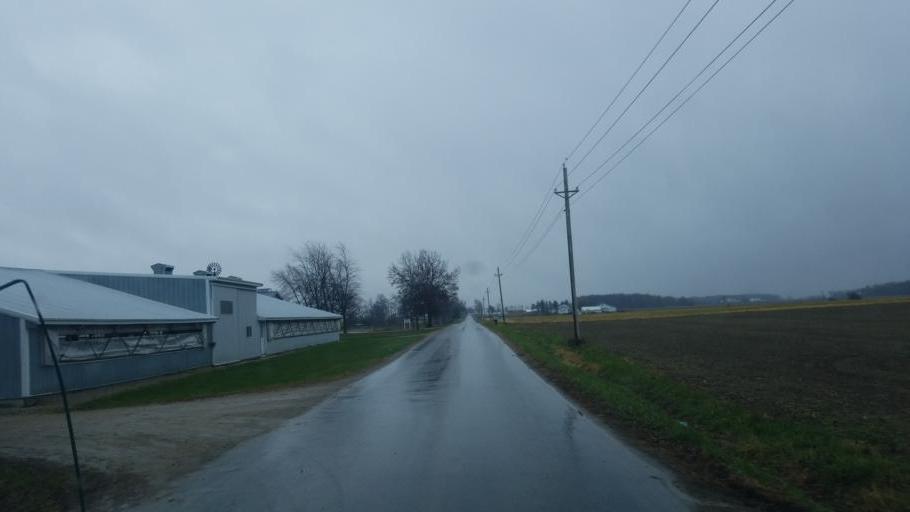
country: US
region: Indiana
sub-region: Adams County
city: Berne
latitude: 40.6491
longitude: -84.8785
